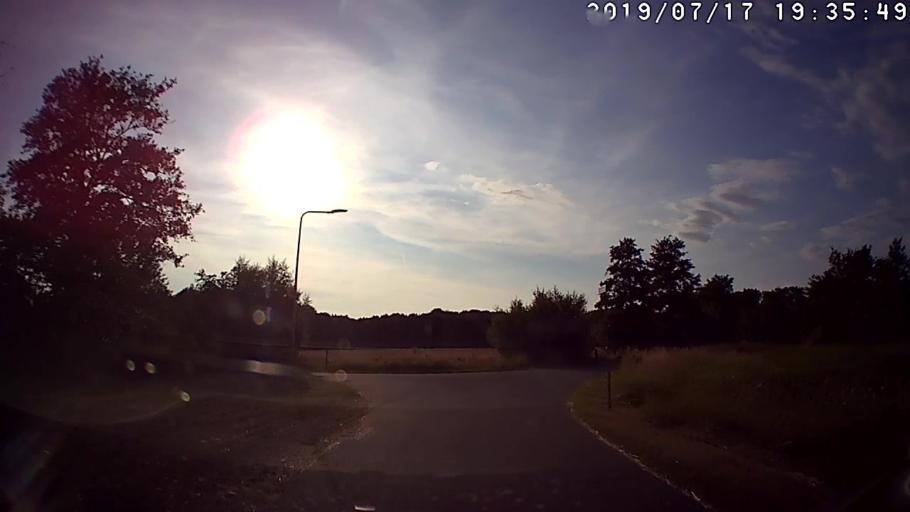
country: NL
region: Overijssel
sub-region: Gemeente Zwolle
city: Zwolle
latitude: 52.5422
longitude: 6.0920
